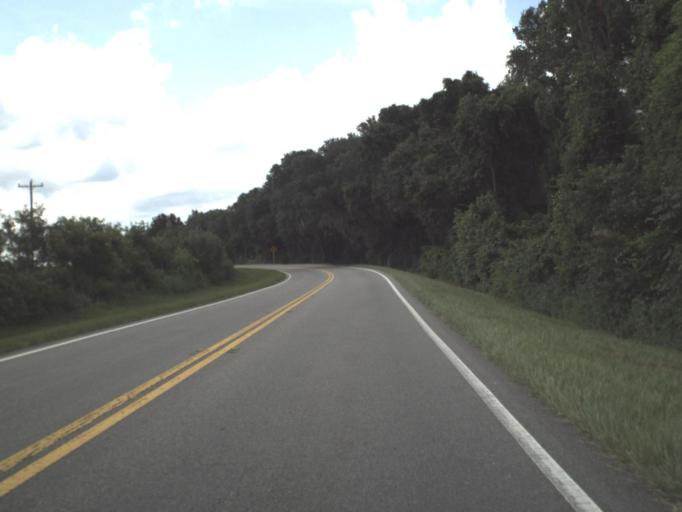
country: US
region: Florida
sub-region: Madison County
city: Madison
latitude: 30.4479
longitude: -83.6264
